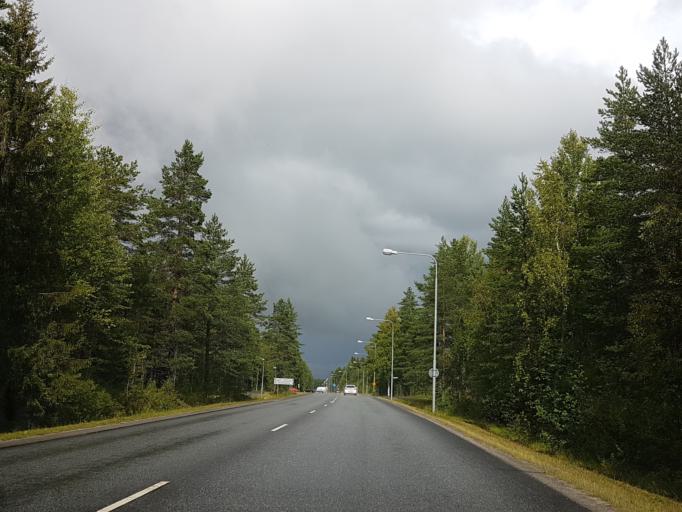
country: SE
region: Vaesterbotten
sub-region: Umea Kommun
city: Ersmark
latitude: 63.8503
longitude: 20.3432
